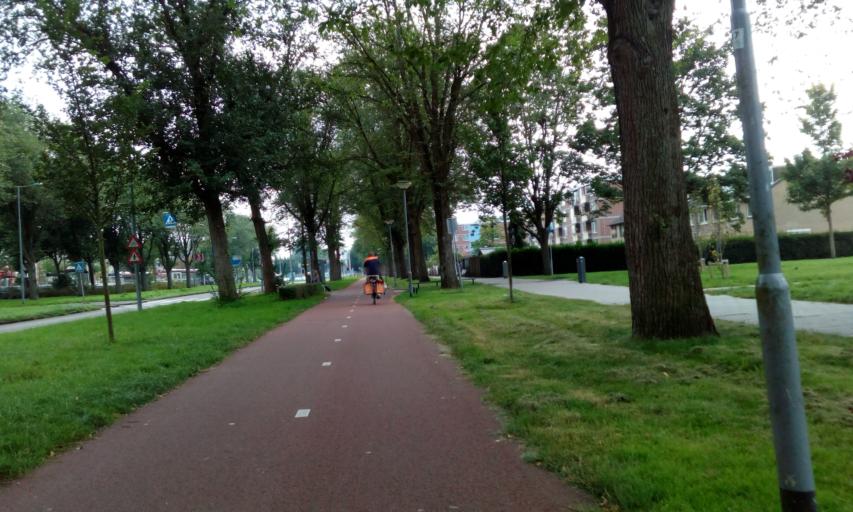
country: NL
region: South Holland
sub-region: Gemeente Rotterdam
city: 's-Gravenland
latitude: 51.9469
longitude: 4.5532
